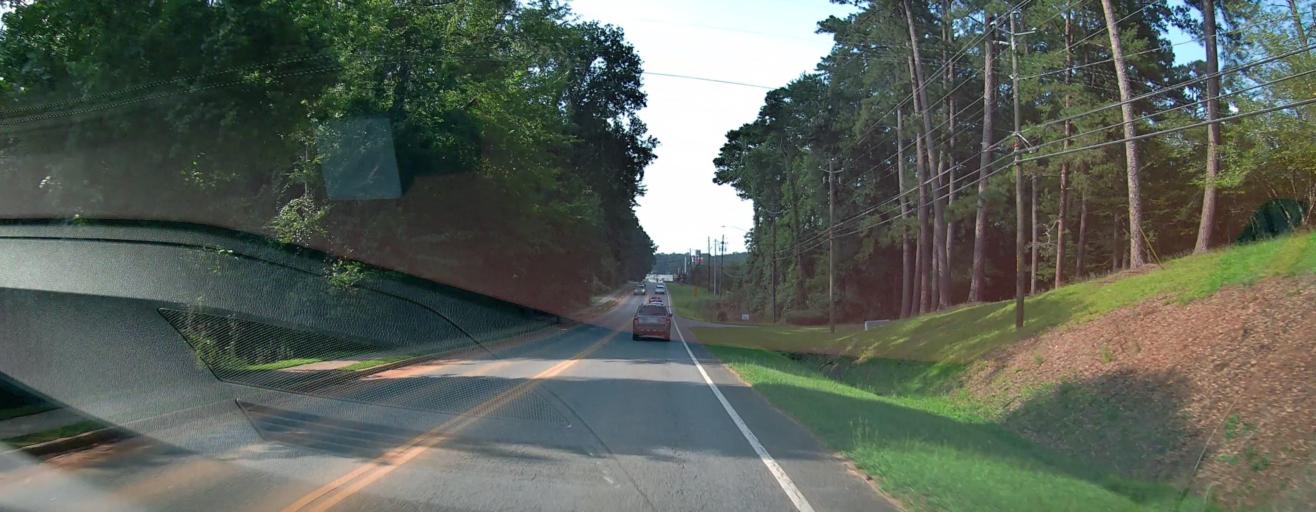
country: US
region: Georgia
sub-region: Bibb County
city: Macon
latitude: 32.8687
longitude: -83.6623
